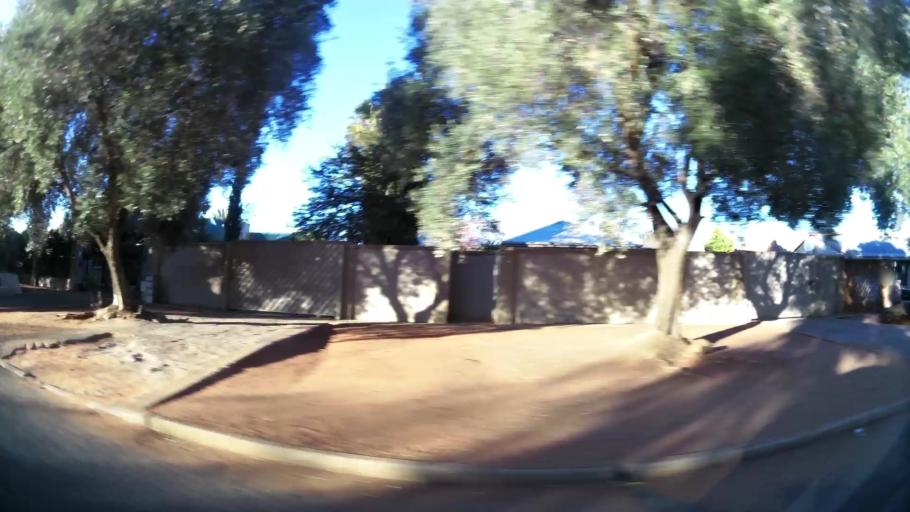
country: ZA
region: Northern Cape
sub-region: Frances Baard District Municipality
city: Kimberley
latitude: -28.7531
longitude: 24.7428
